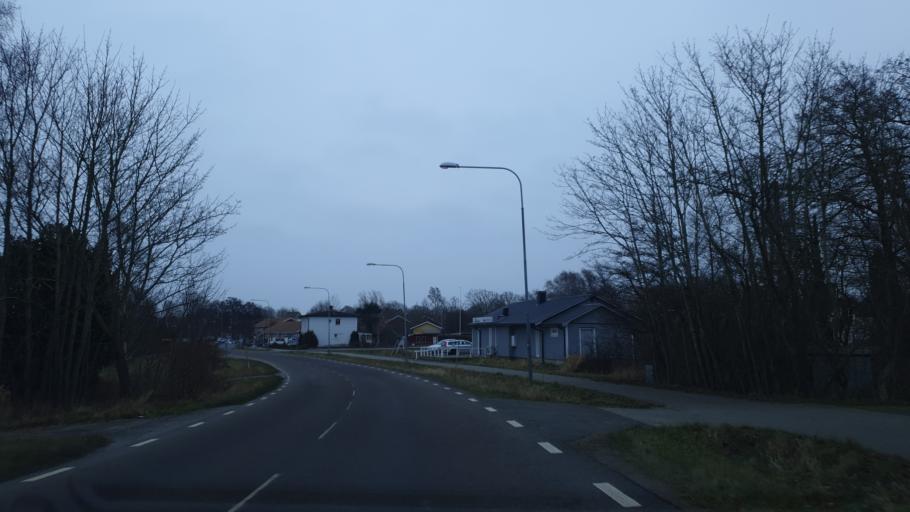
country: SE
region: Blekinge
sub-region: Karlskrona Kommun
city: Sturko
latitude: 56.1135
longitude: 15.6746
